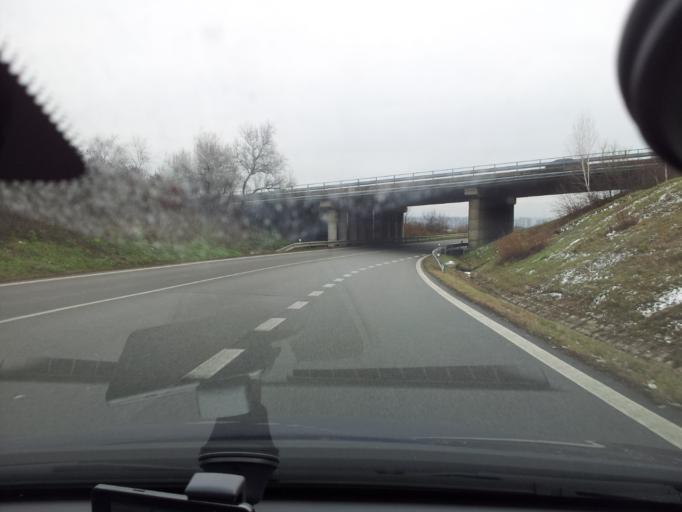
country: SK
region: Kosicky
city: Kosice
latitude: 48.7887
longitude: 21.3087
